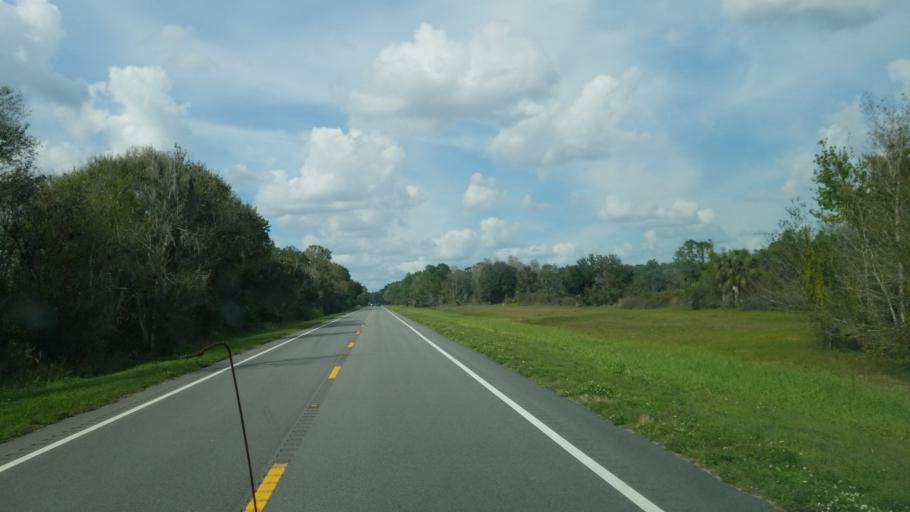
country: US
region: Florida
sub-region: Indian River County
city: Fellsmere
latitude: 27.7844
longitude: -80.9279
